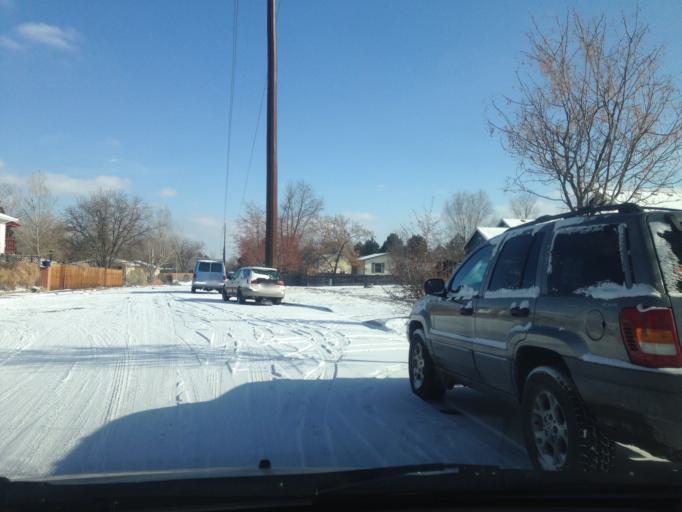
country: US
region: Colorado
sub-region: Boulder County
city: Lafayette
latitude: 39.9906
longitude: -105.0959
